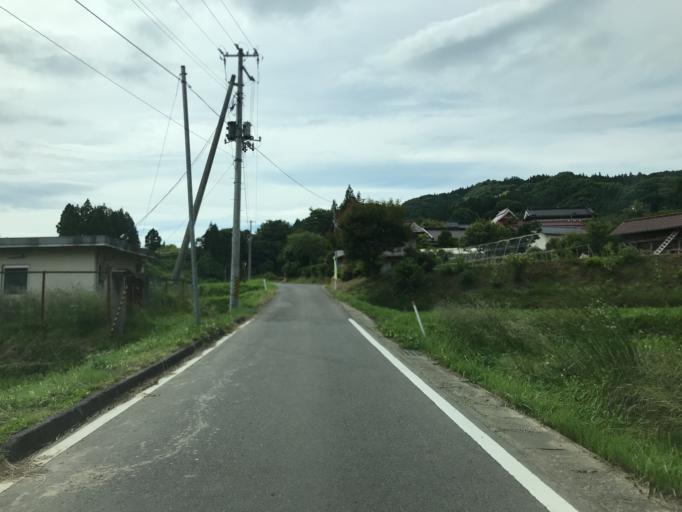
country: JP
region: Fukushima
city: Funehikimachi-funehiki
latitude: 37.4593
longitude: 140.6400
